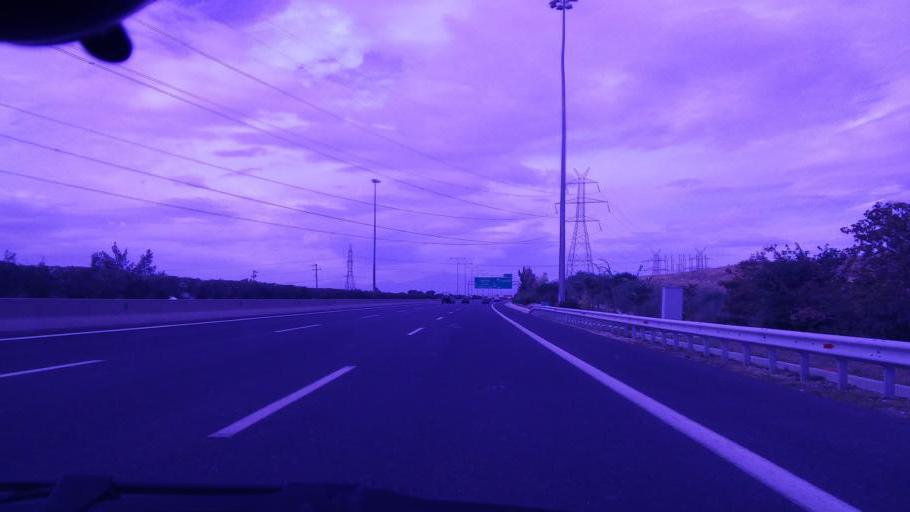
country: GR
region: Attica
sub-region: Nomarchia Dytikis Attikis
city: Fyli
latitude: 38.0869
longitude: 23.6406
